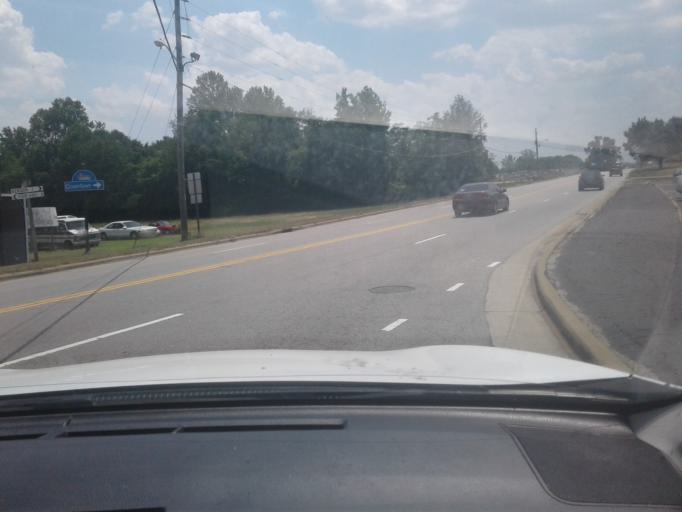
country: US
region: North Carolina
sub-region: Johnston County
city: Benson
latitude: 35.3886
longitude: -78.5435
